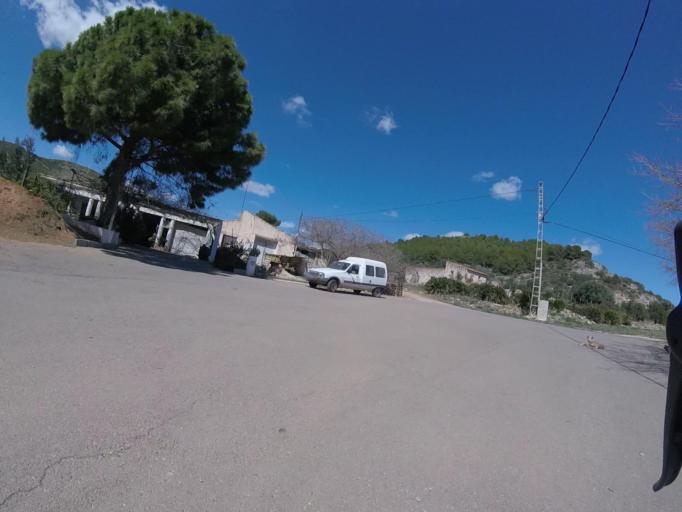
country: ES
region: Valencia
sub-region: Provincia de Castello
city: Torreblanca
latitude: 40.1698
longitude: 0.1581
